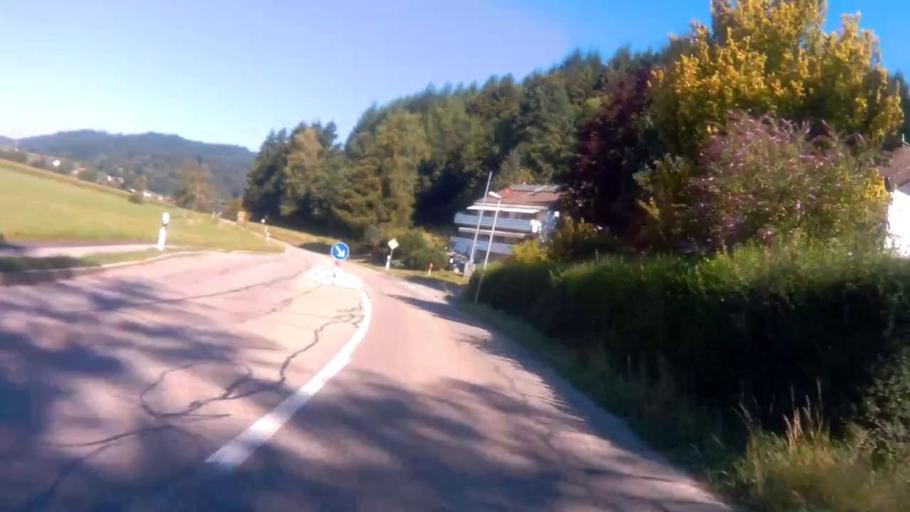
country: DE
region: Baden-Wuerttemberg
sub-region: Freiburg Region
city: Hausen
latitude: 47.6829
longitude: 7.8078
